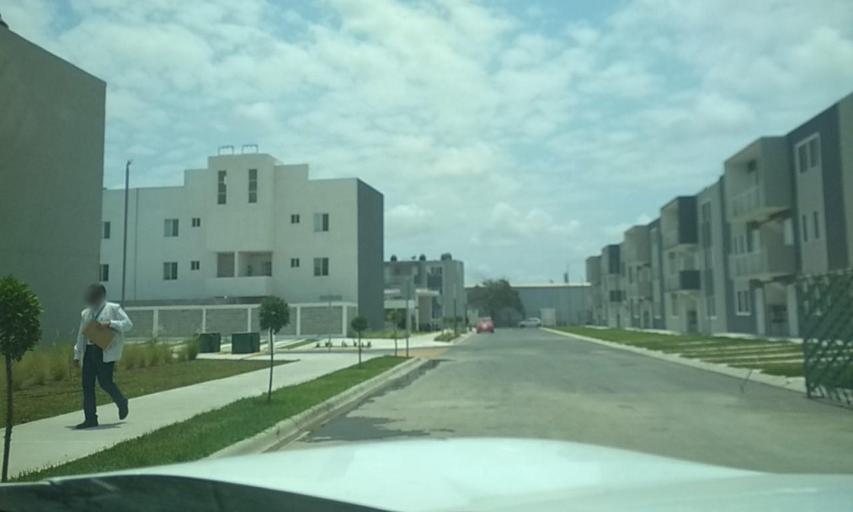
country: MX
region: Veracruz
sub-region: Veracruz
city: Las Amapolas
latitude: 19.1475
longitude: -96.2160
